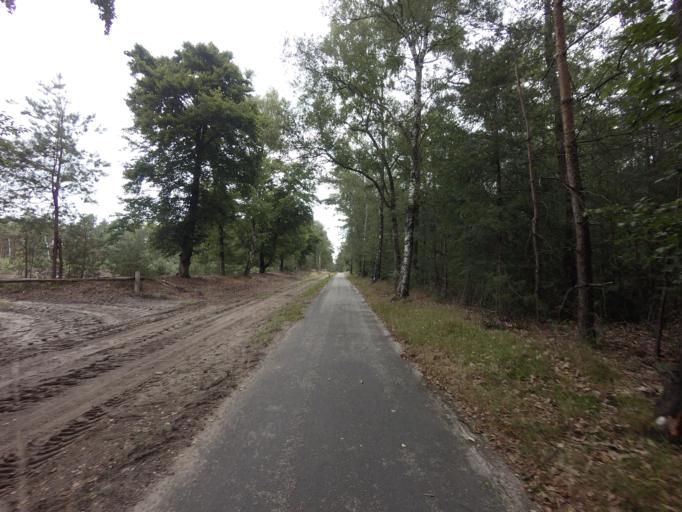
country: NL
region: Overijssel
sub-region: Gemeente Hof van Twente
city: Markelo
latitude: 52.3140
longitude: 6.4505
